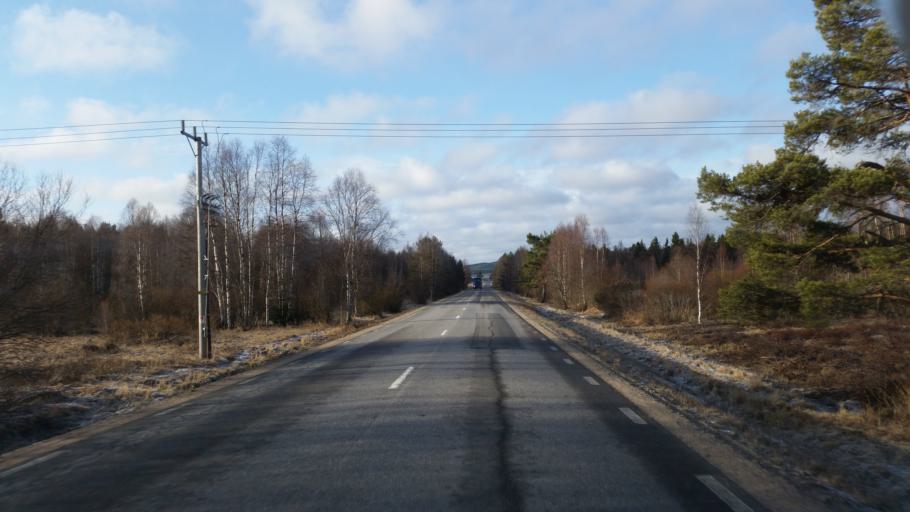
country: SE
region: Gaevleborg
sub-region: Ljusdals Kommun
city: Farila
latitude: 61.7855
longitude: 15.8274
